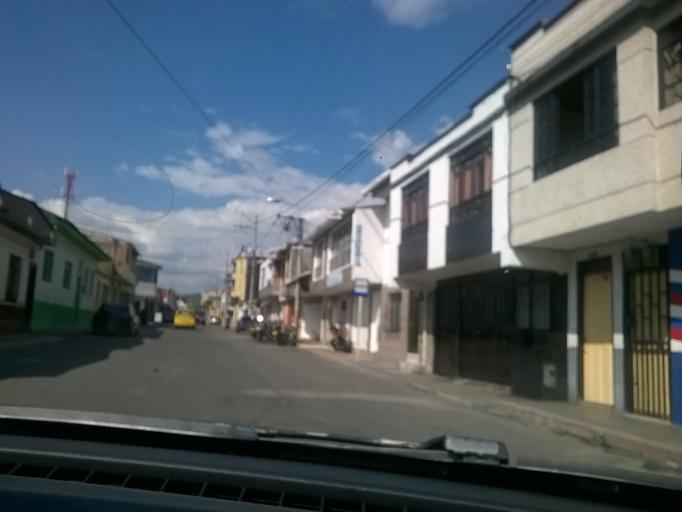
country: CO
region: Quindio
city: Calarca
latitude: 4.5251
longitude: -75.6422
